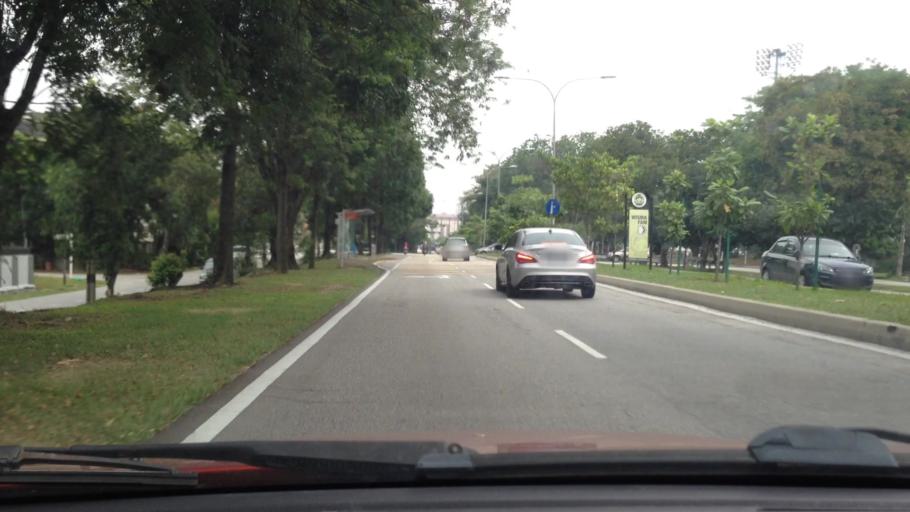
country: MY
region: Selangor
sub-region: Petaling
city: Petaling Jaya
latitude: 3.0967
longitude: 101.6072
